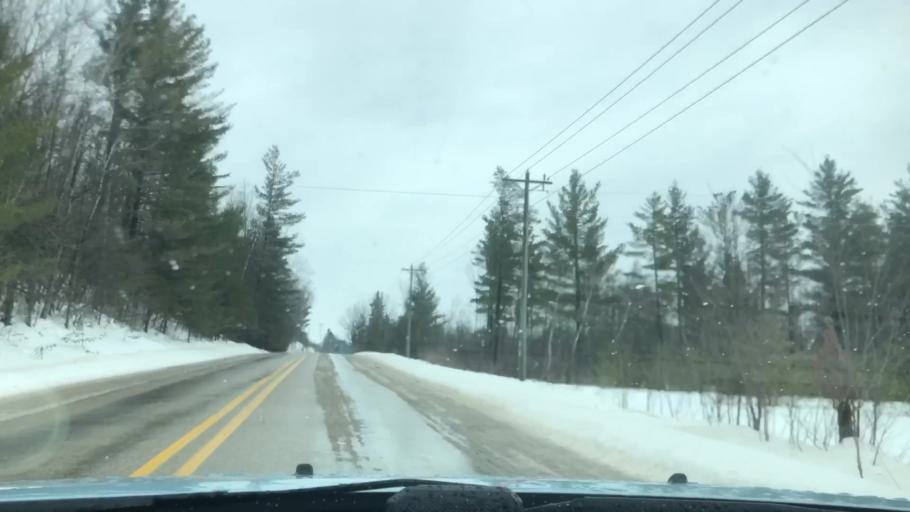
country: US
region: Michigan
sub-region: Charlevoix County
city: East Jordan
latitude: 45.1080
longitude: -85.1288
